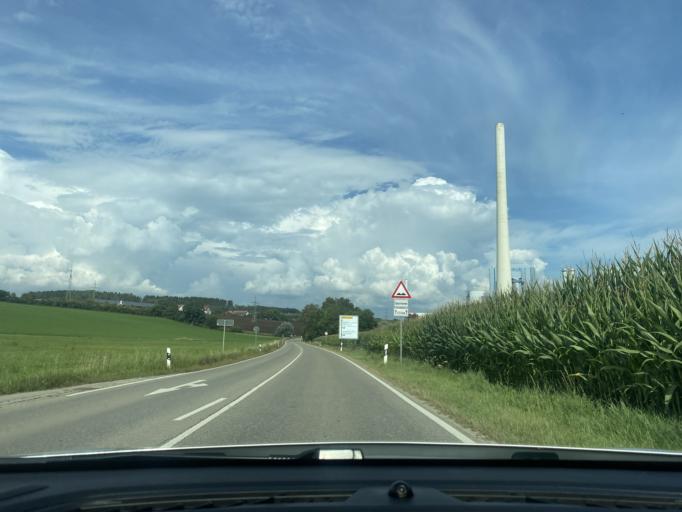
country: DE
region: Bavaria
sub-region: Upper Bavaria
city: Zolling
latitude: 48.4543
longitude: 11.7925
